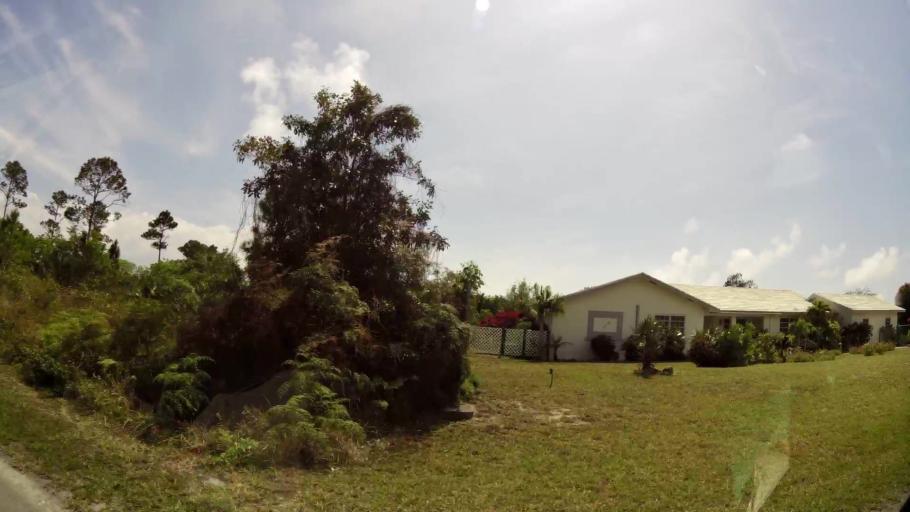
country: BS
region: Freeport
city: Freeport
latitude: 26.5070
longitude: -78.7238
